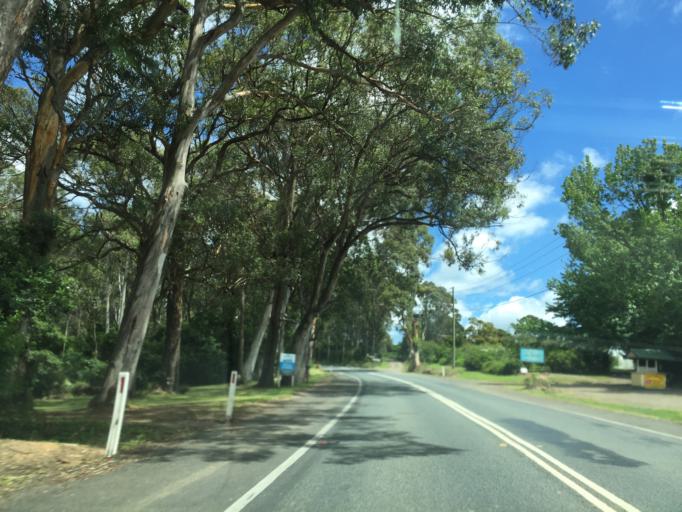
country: AU
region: New South Wales
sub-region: Hawkesbury
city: Richmond
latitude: -33.5028
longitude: 150.5411
